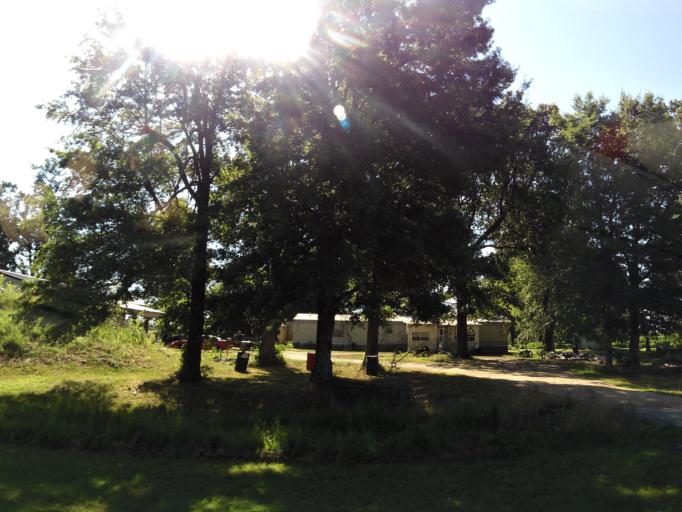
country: US
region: Arkansas
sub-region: Clay County
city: Corning
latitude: 36.4021
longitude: -90.5080
